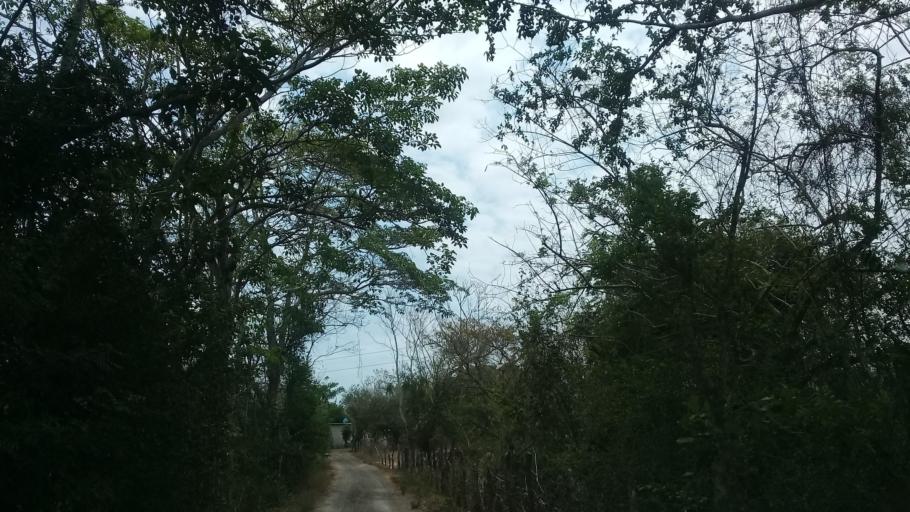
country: MX
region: Veracruz
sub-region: Veracruz
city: Delfino Victoria (Santa Fe)
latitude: 19.1756
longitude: -96.3039
